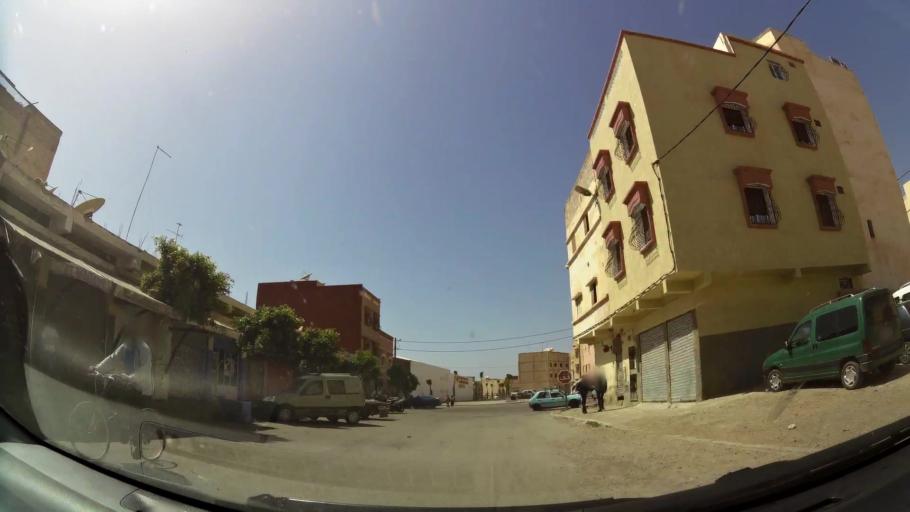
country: MA
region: Souss-Massa-Draa
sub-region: Inezgane-Ait Mellou
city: Inezgane
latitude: 30.3478
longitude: -9.5380
